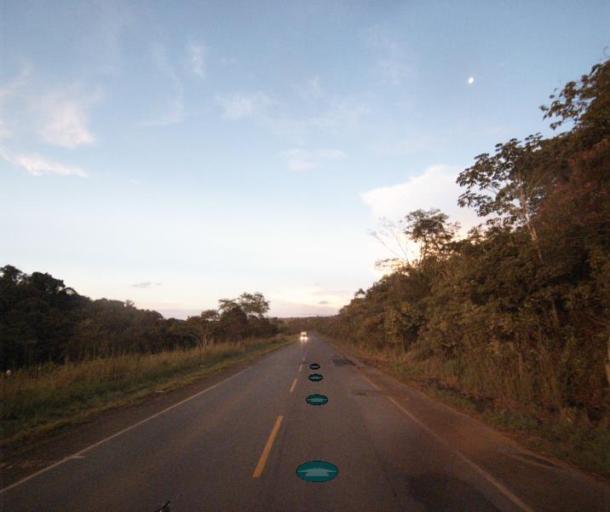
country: BR
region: Goias
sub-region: Pirenopolis
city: Pirenopolis
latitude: -15.9900
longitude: -48.8339
